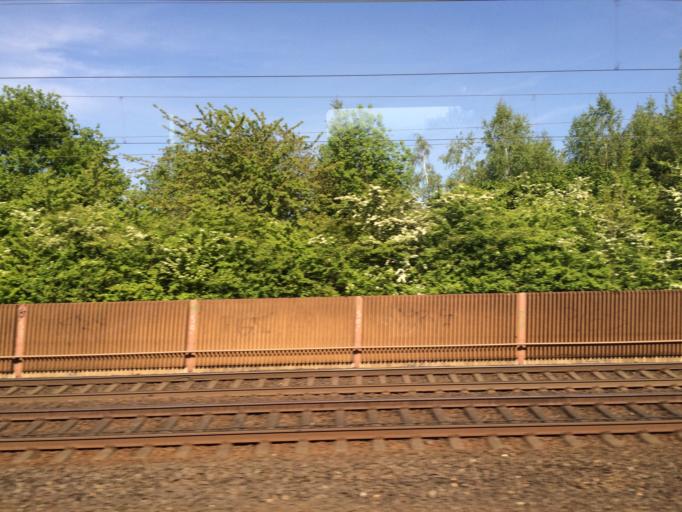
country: DE
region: North Rhine-Westphalia
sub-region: Regierungsbezirk Koln
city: Leverkusen
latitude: 51.0486
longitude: 6.9873
